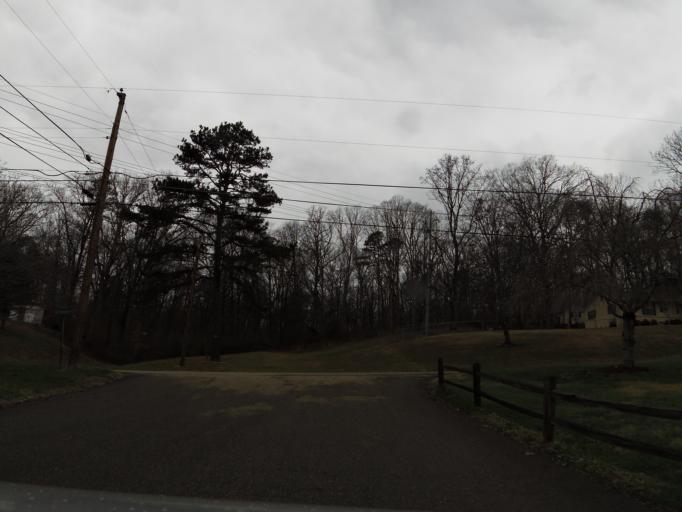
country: US
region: Tennessee
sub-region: Knox County
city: Knoxville
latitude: 35.9885
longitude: -84.0229
